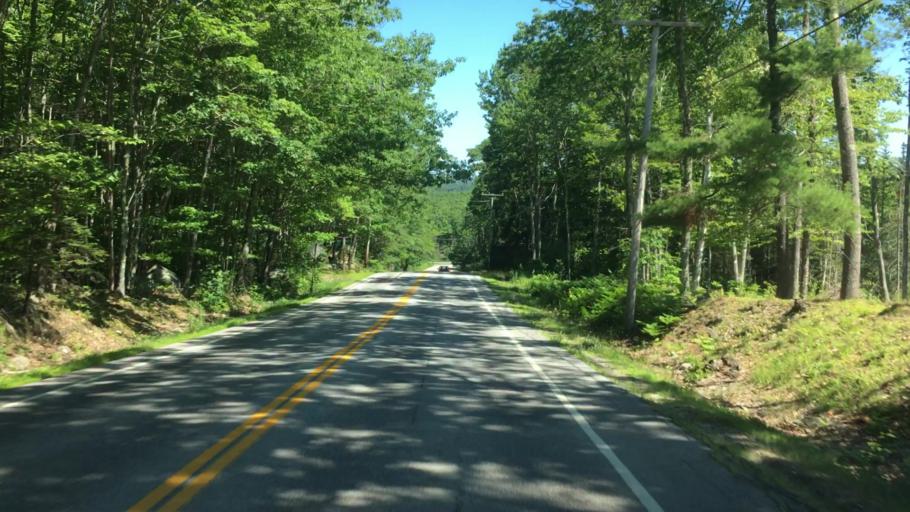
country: US
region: Maine
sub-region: Hancock County
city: Sedgwick
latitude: 44.3438
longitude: -68.6736
